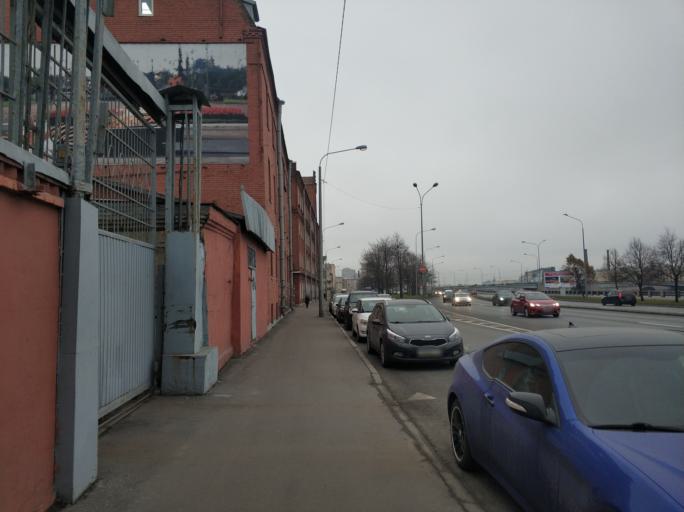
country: RU
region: Leningrad
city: Sampsonievskiy
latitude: 59.9721
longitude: 30.3353
